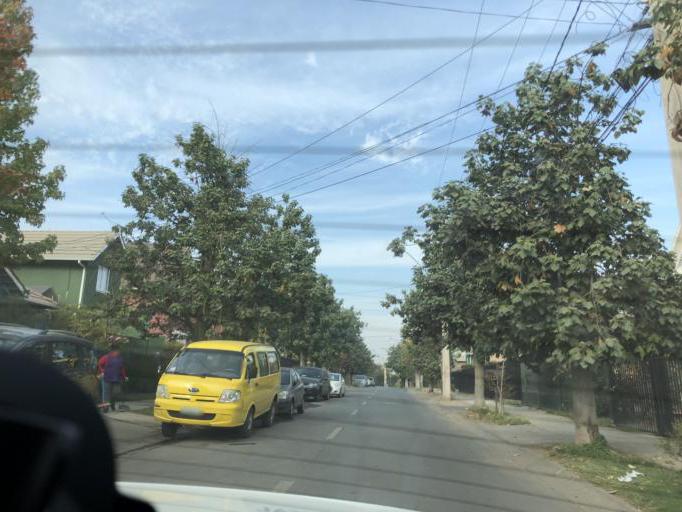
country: CL
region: Santiago Metropolitan
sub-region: Provincia de Cordillera
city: Puente Alto
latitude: -33.5632
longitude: -70.5472
